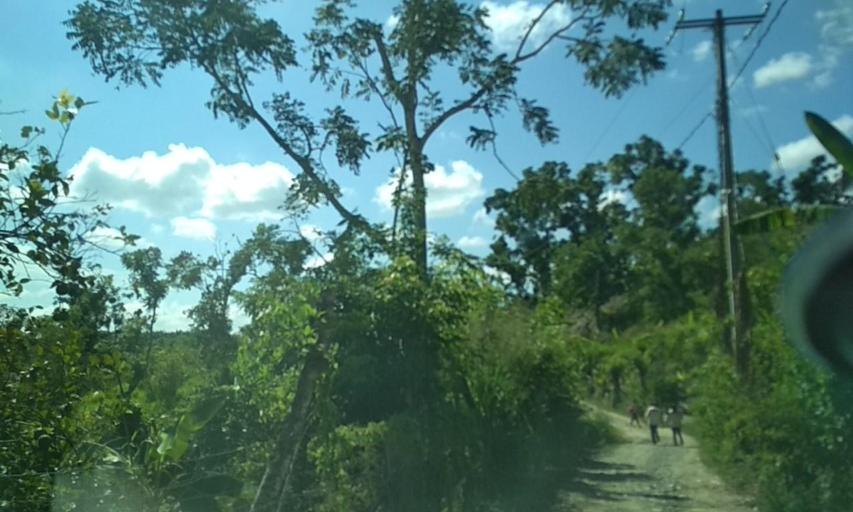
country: MX
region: Veracruz
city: Cazones de Herrera
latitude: 20.6235
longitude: -97.3261
